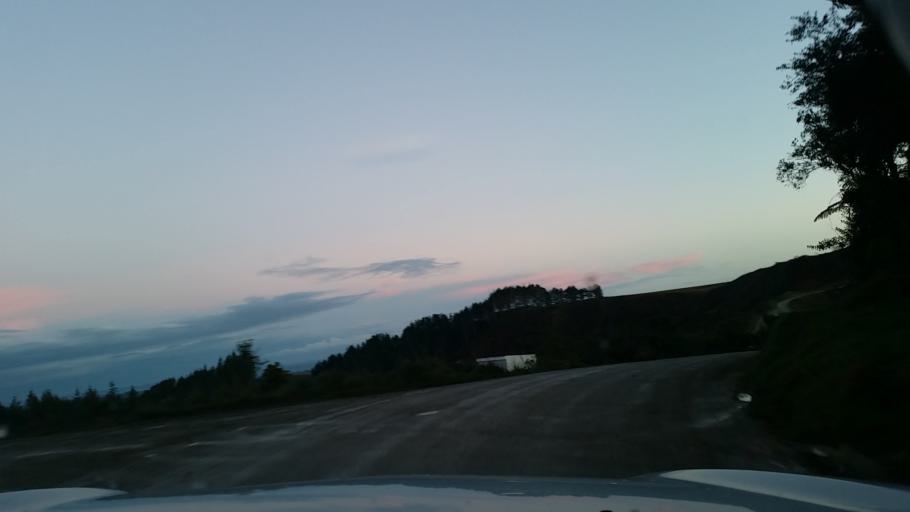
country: NZ
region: Manawatu-Wanganui
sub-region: Wanganui District
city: Wanganui
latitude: -39.7704
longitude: 174.8721
